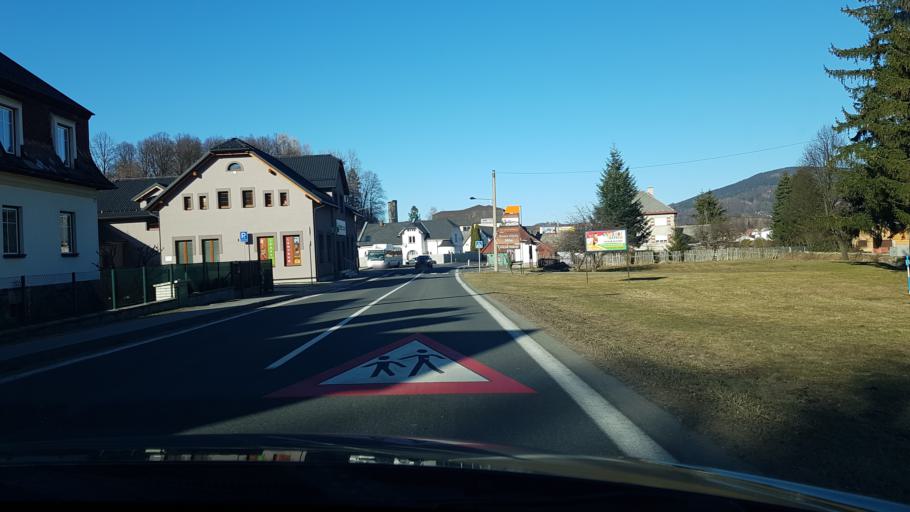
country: CZ
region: Olomoucky
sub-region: Okres Jesenik
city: Jesenik
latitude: 50.1981
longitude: 17.1937
